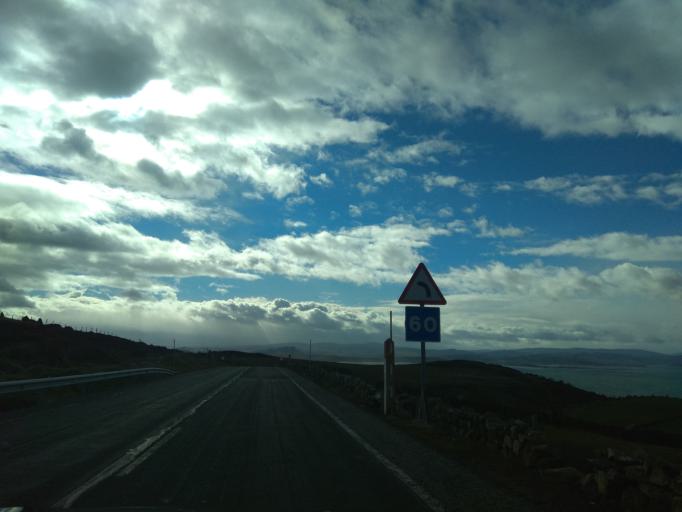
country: ES
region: Castille and Leon
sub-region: Provincia de Burgos
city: Arija
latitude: 43.0450
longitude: -3.8779
